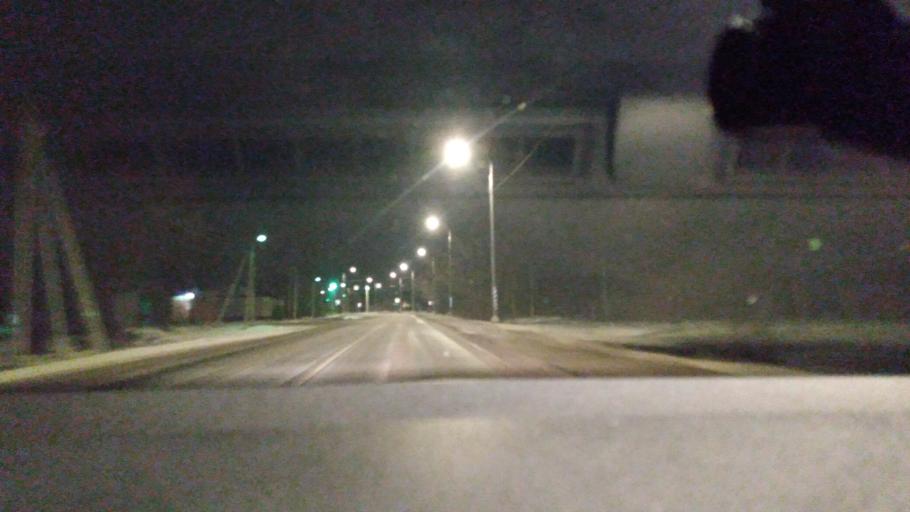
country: RU
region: Moskovskaya
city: Krasnaya Poyma
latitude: 55.1060
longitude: 39.0063
